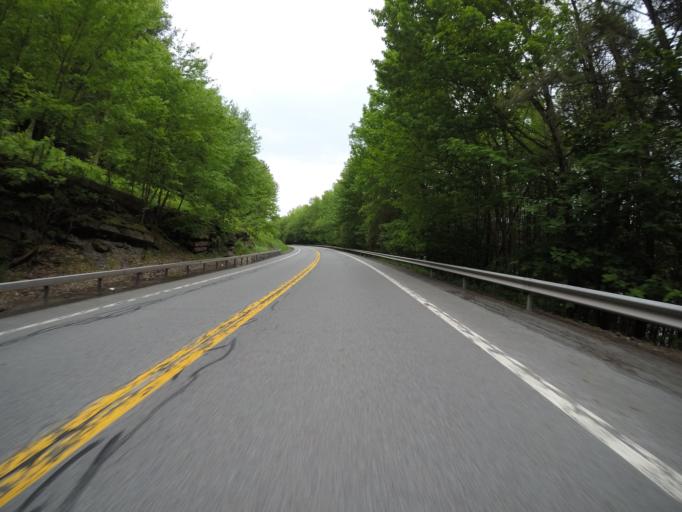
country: US
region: New York
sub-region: Sullivan County
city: Livingston Manor
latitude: 42.0730
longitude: -74.8887
